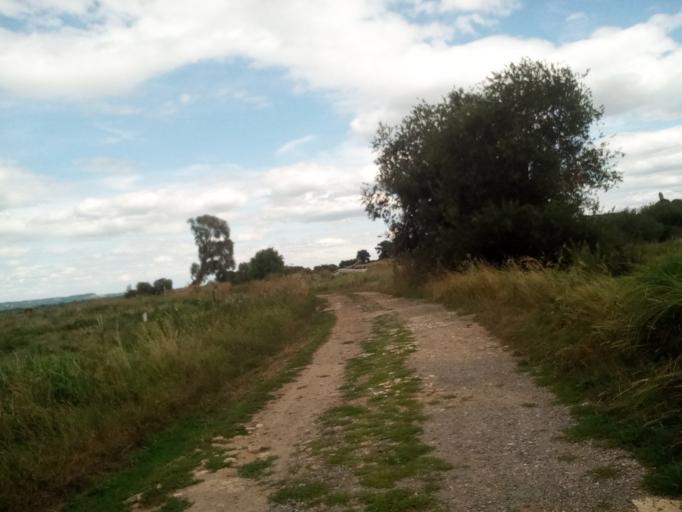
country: FR
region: Lower Normandy
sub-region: Departement du Calvados
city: Troarn
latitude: 49.1713
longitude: -0.1445
